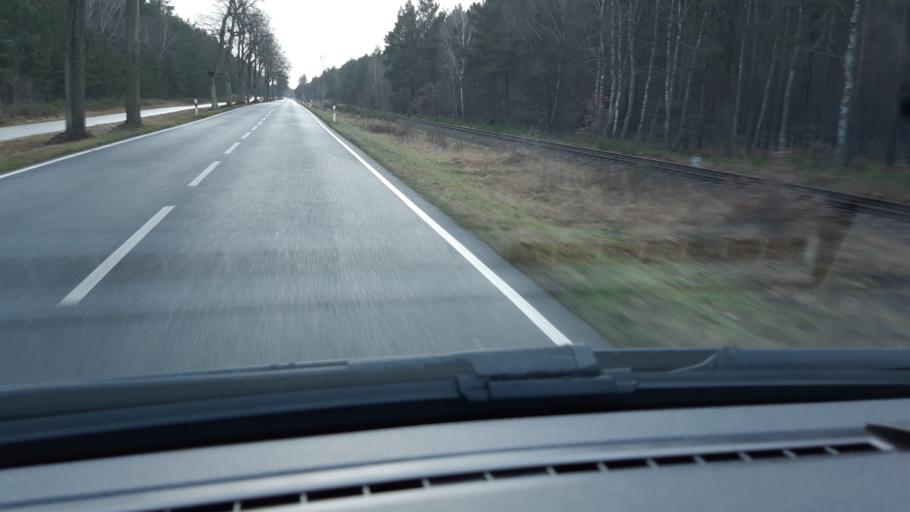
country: DE
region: Brandenburg
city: Zehdenick
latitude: 53.0278
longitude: 13.3807
